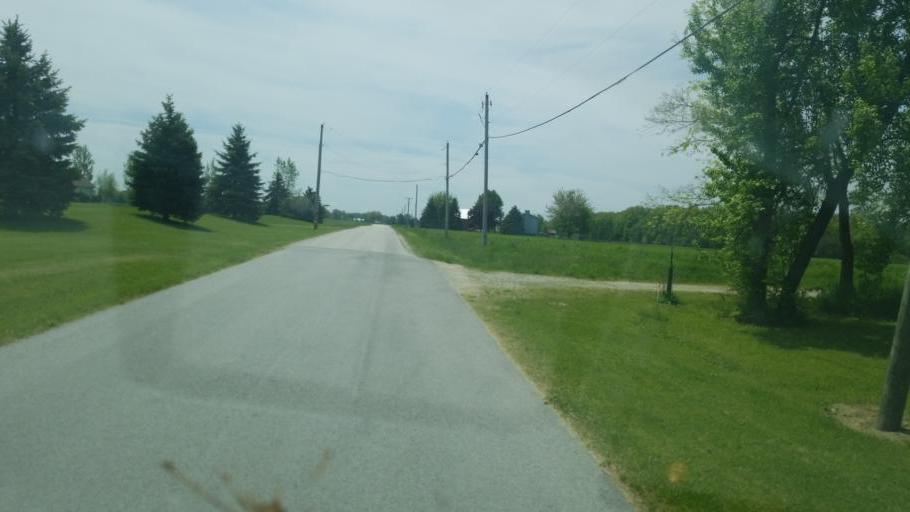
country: US
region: Ohio
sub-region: Ottawa County
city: Oak Harbor
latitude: 41.4961
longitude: -83.1643
